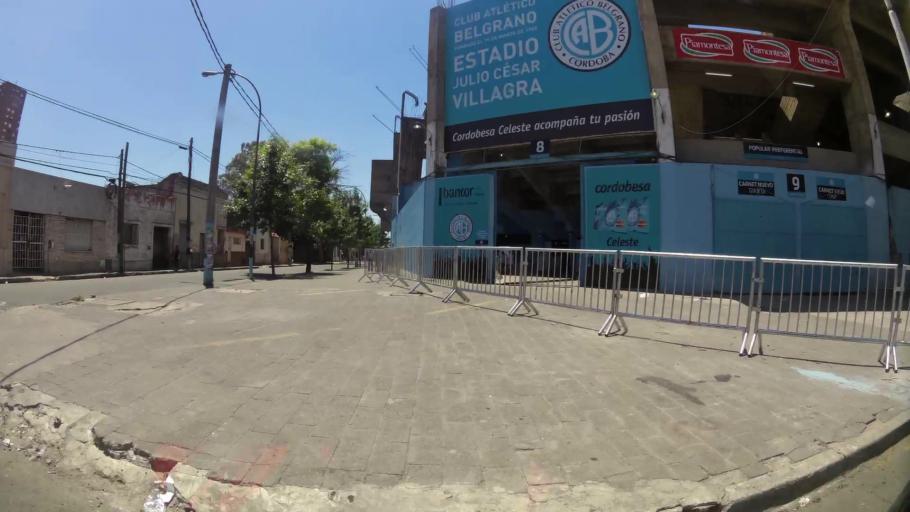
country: AR
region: Cordoba
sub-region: Departamento de Capital
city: Cordoba
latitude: -31.4043
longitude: -64.2072
